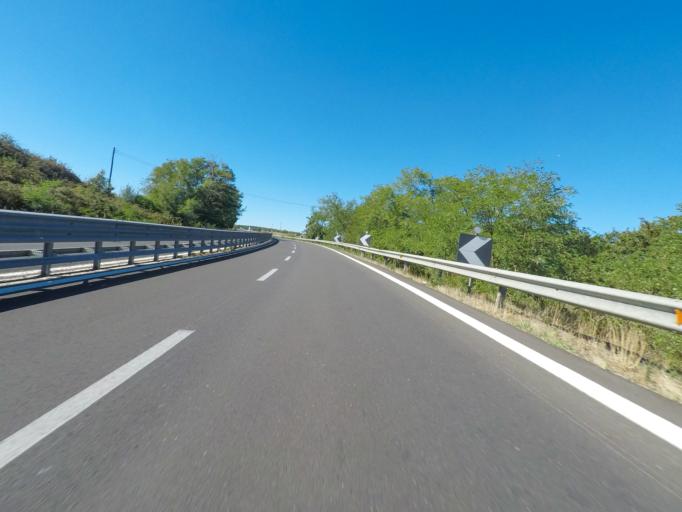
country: IT
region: Latium
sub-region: Provincia di Viterbo
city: Montalto di Castro
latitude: 42.3247
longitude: 11.6391
